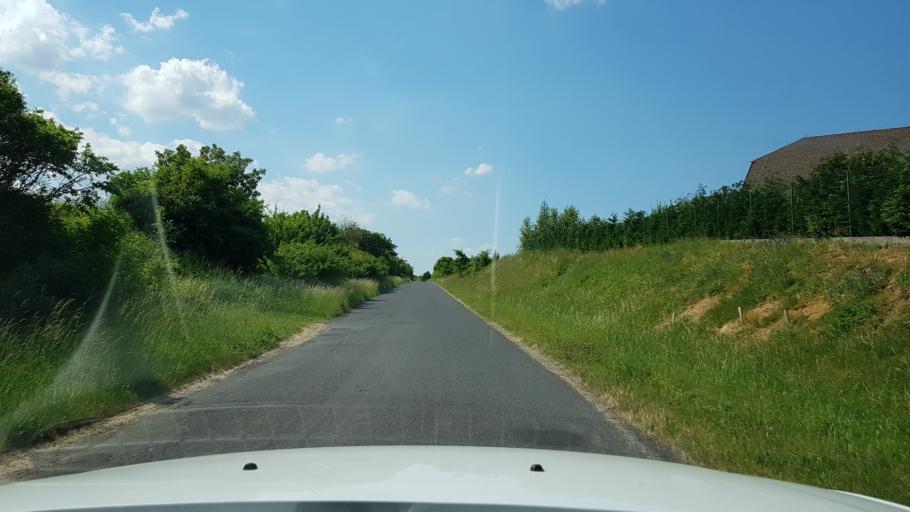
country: PL
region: West Pomeranian Voivodeship
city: Trzcinsko Zdroj
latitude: 52.9892
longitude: 14.6016
